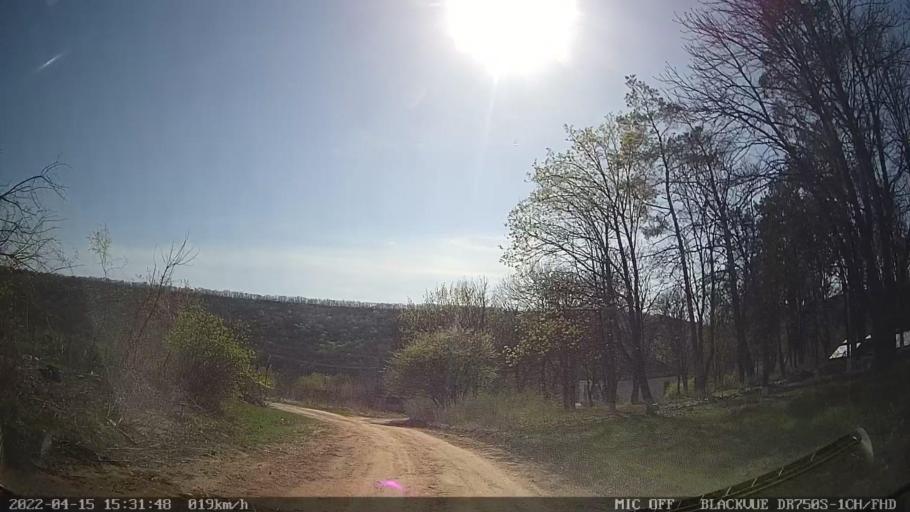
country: MD
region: Raionul Ocnita
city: Otaci
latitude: 48.3519
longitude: 27.9194
